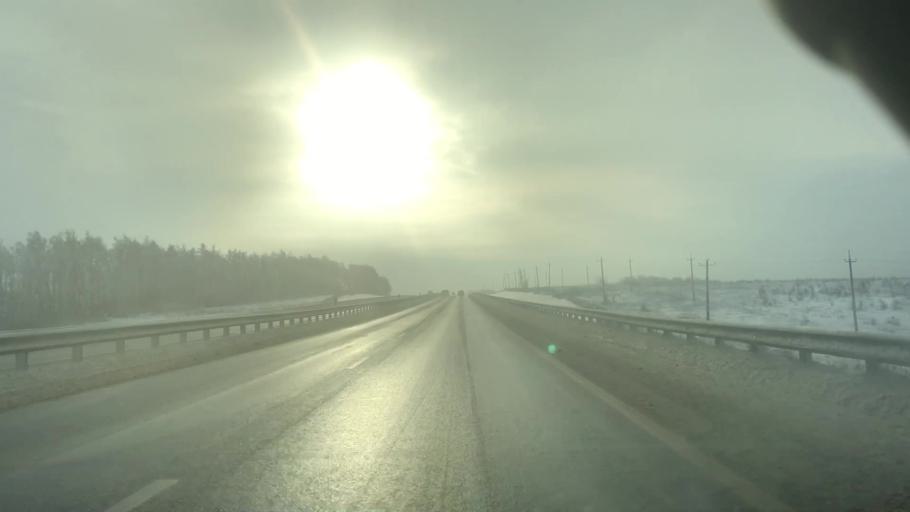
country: RU
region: Tula
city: Venev
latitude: 54.3186
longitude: 38.1544
